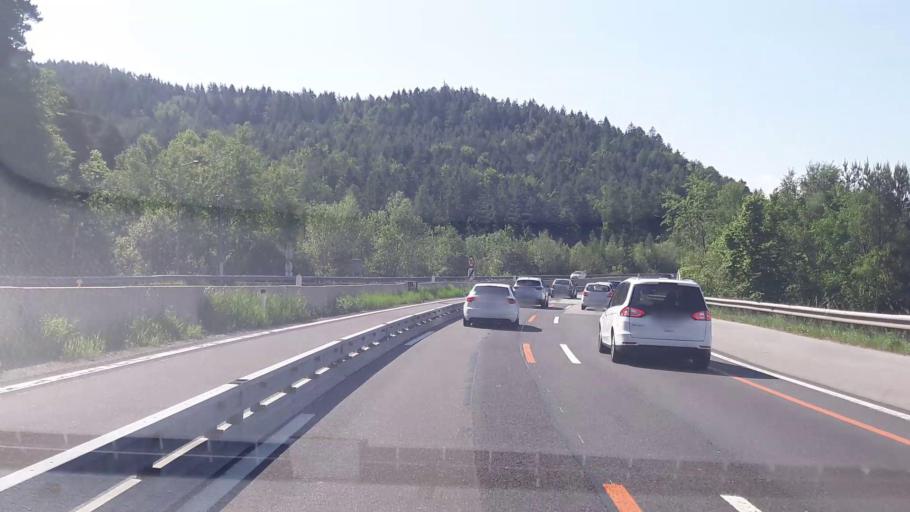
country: AT
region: Lower Austria
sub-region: Politischer Bezirk Neunkirchen
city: Thomasberg
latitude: 47.5703
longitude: 16.1142
